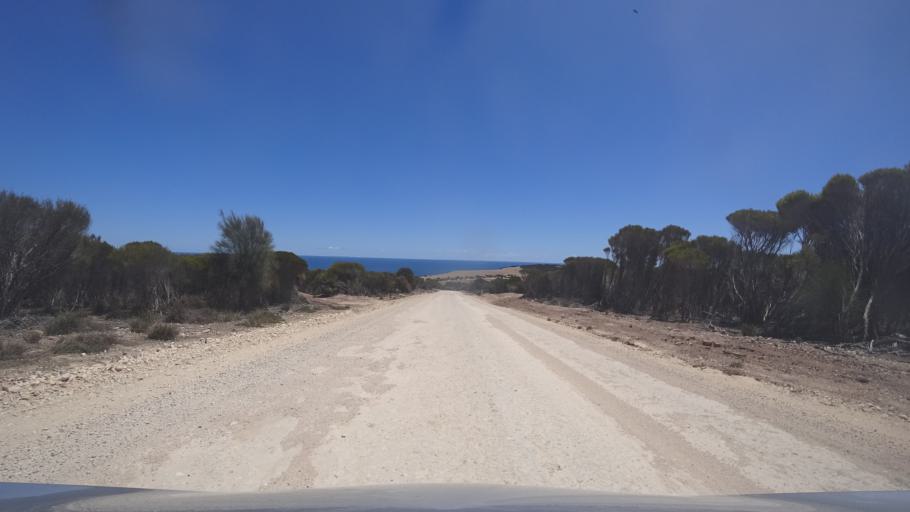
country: AU
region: South Australia
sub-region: Kangaroo Island
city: Kingscote
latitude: -35.6303
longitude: 137.2134
